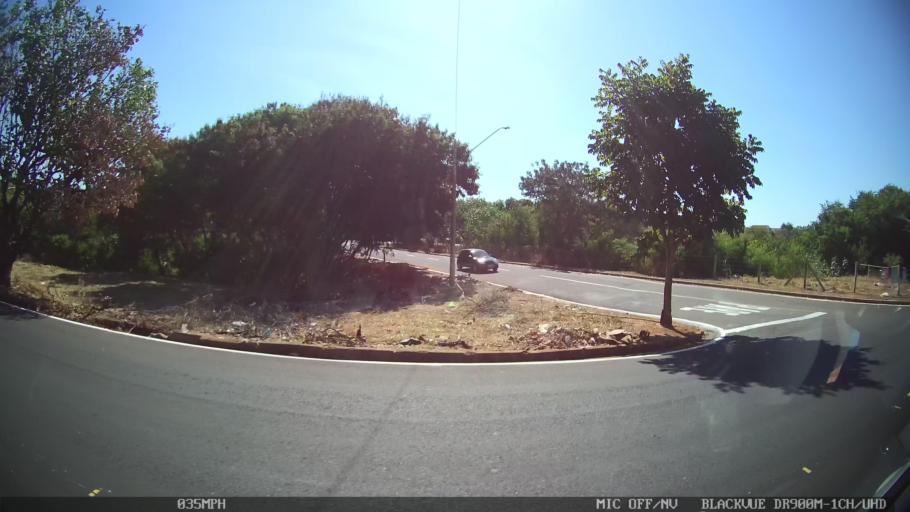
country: BR
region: Sao Paulo
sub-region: Sao Jose Do Rio Preto
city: Sao Jose do Rio Preto
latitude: -20.7739
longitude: -49.4079
